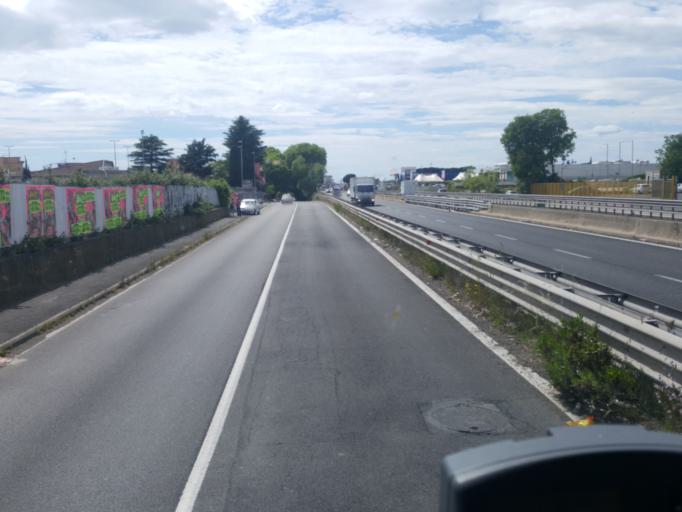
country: IT
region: Latium
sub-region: Citta metropolitana di Roma Capitale
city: La Massimina-Casal Lumbroso
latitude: 41.8819
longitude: 12.3547
